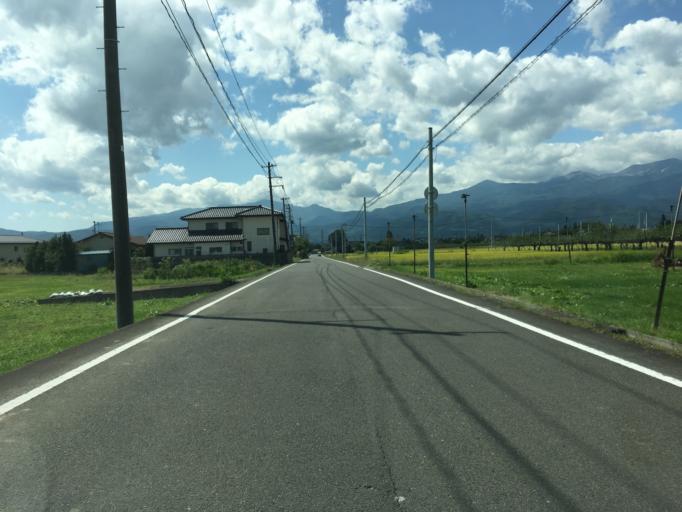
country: JP
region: Fukushima
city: Fukushima-shi
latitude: 37.7611
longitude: 140.4152
